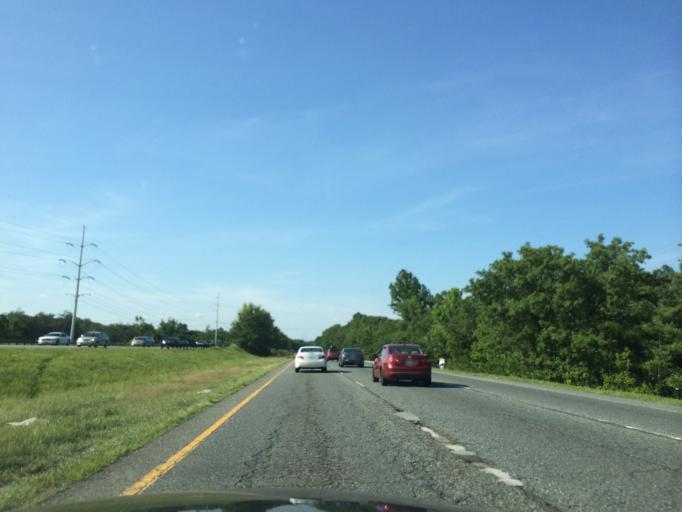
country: US
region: Maryland
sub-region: Anne Arundel County
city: Crofton
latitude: 39.0010
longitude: -76.7001
